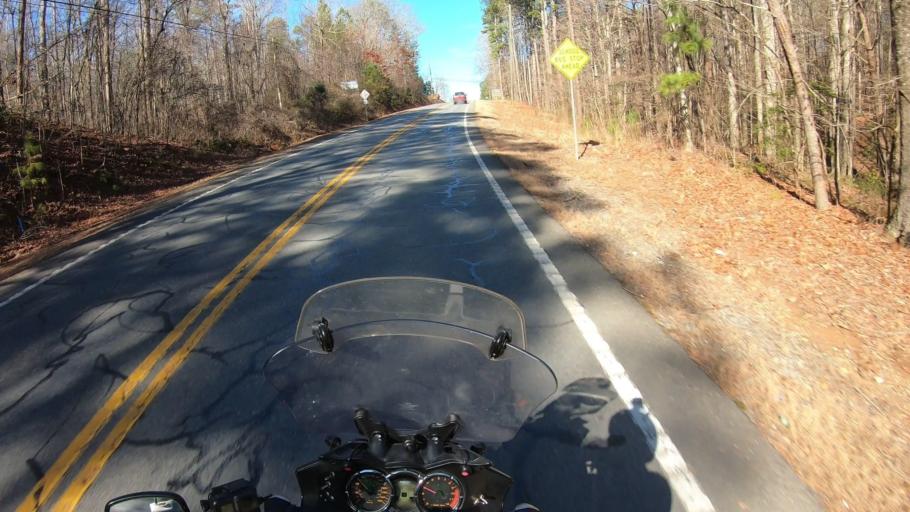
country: US
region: Georgia
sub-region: Gilmer County
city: Ellijay
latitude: 34.6019
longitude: -84.5940
